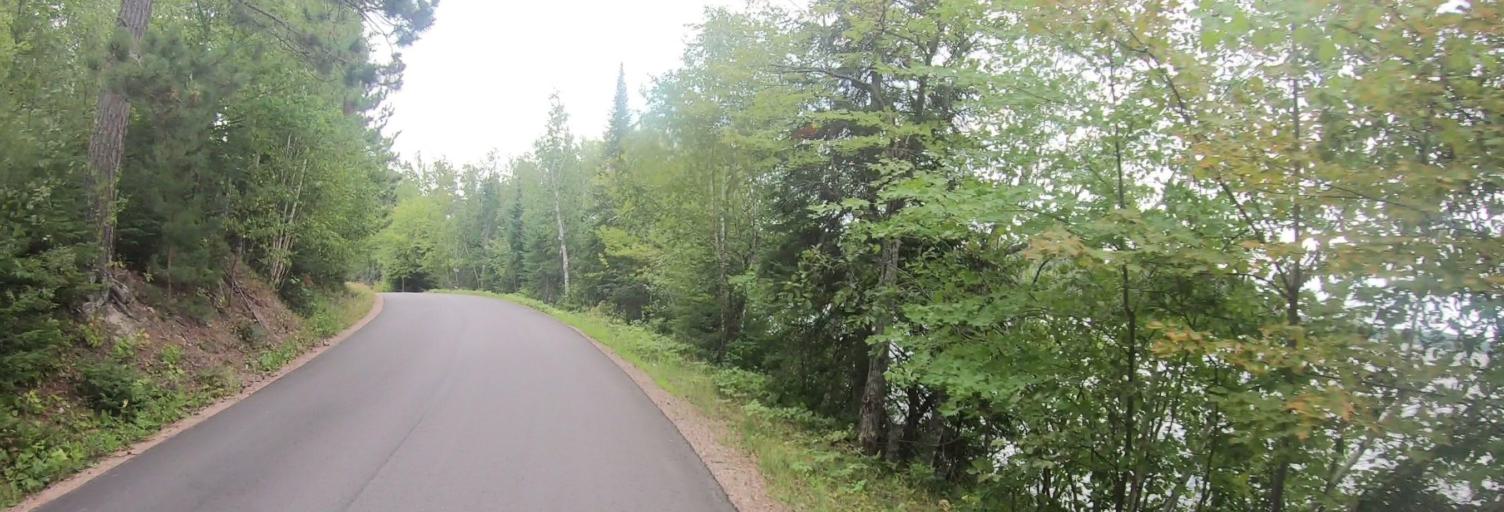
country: US
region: Minnesota
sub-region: Saint Louis County
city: Mountain Iron
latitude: 47.9509
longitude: -92.6228
